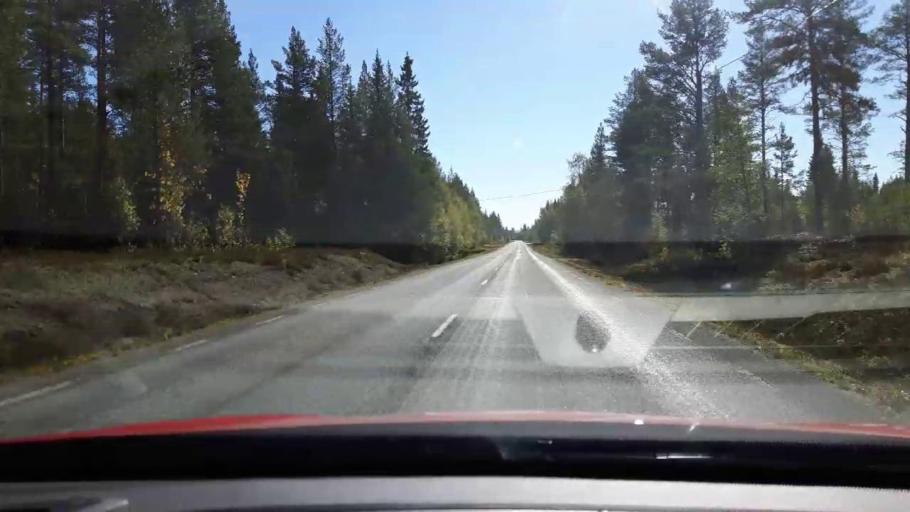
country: SE
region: Jaemtland
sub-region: Harjedalens Kommun
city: Sveg
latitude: 62.3704
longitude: 13.9849
